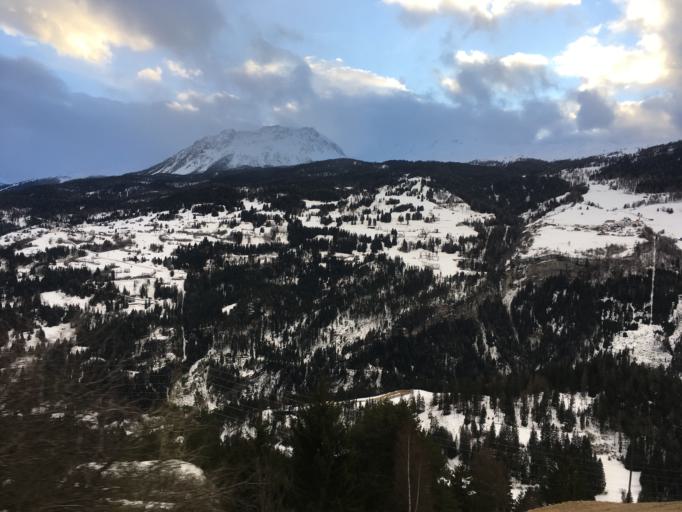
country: CH
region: Grisons
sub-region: Albula District
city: Tiefencastel
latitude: 46.6759
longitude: 9.5684
